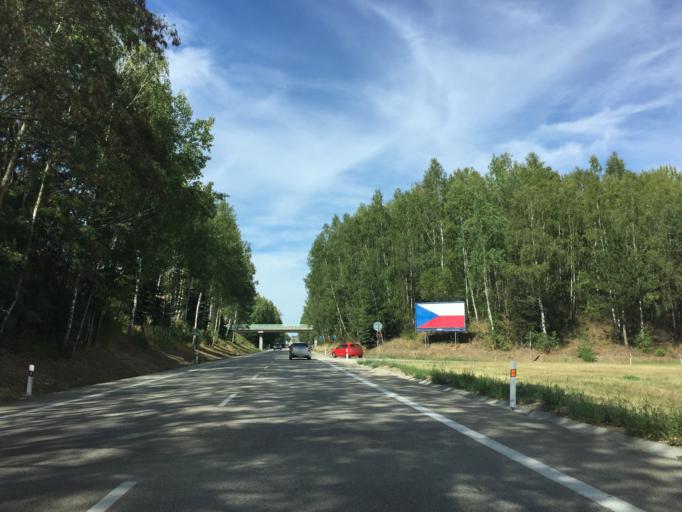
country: CZ
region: Central Bohemia
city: Votice
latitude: 49.6596
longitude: 14.6342
